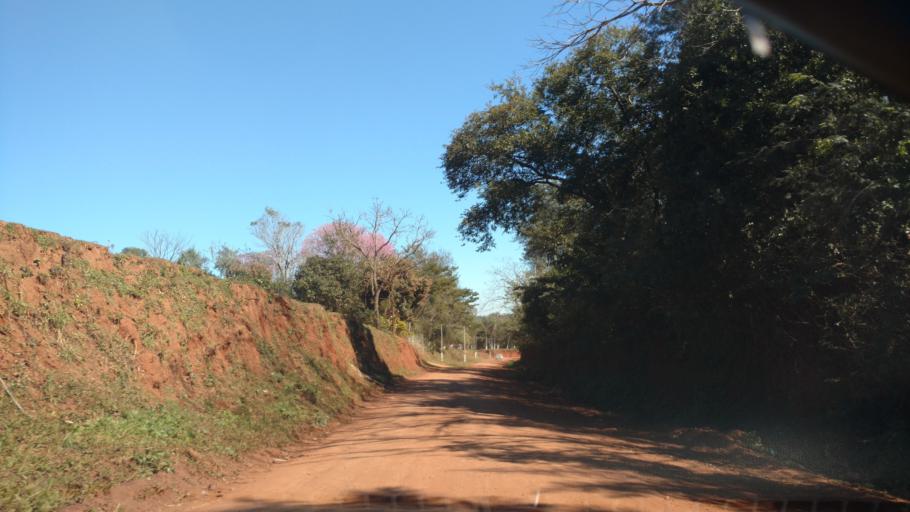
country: PY
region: Paraguari
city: Yaguaron
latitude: -25.5642
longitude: -57.3008
